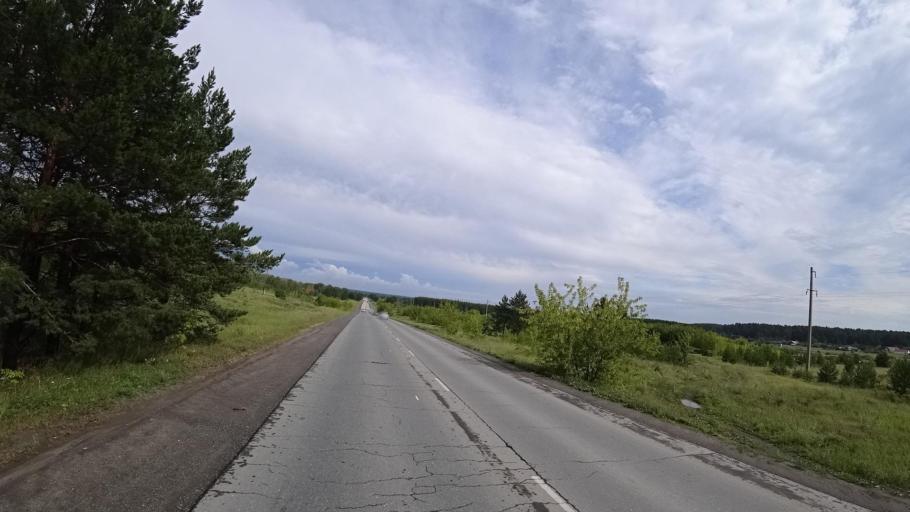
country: RU
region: Sverdlovsk
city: Kamyshlov
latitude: 56.8441
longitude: 62.7711
